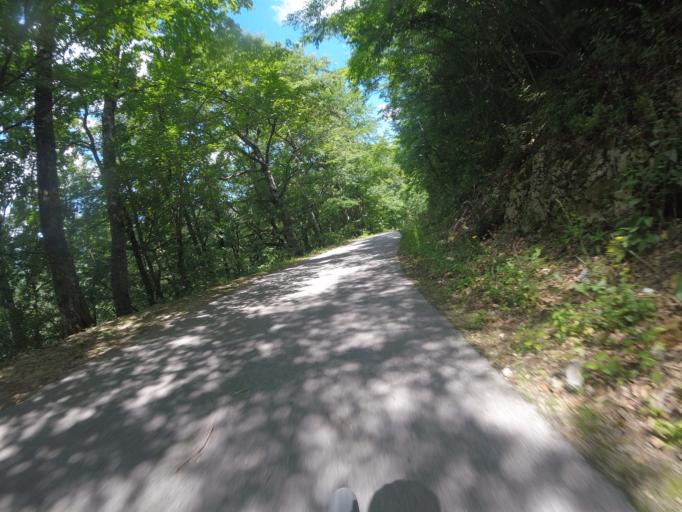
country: SI
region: Kostanjevica na Krki
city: Kostanjevica na Krki
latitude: 45.7647
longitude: 15.4198
